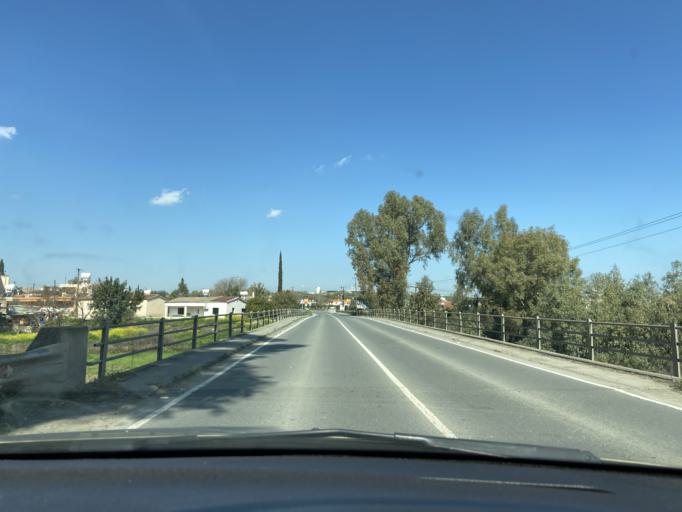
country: CY
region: Lefkosia
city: Dali
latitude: 35.0190
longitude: 33.3951
